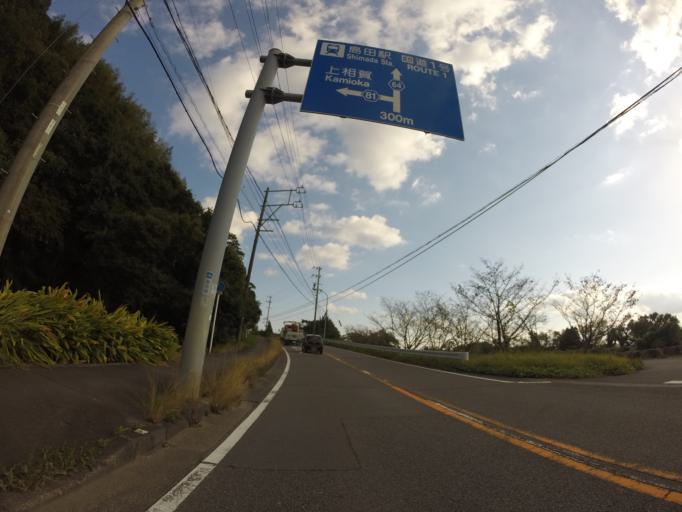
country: JP
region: Shizuoka
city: Kanaya
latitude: 34.8628
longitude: 138.1280
